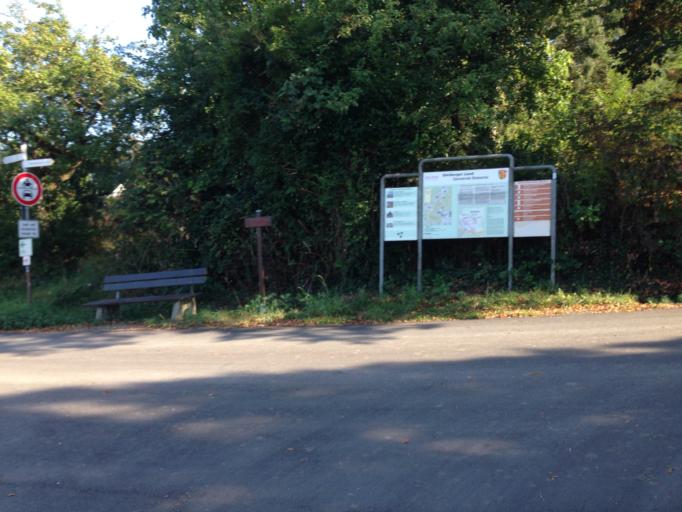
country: DE
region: Hesse
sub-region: Regierungsbezirk Giessen
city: Heuchelheim
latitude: 50.6226
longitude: 8.6161
